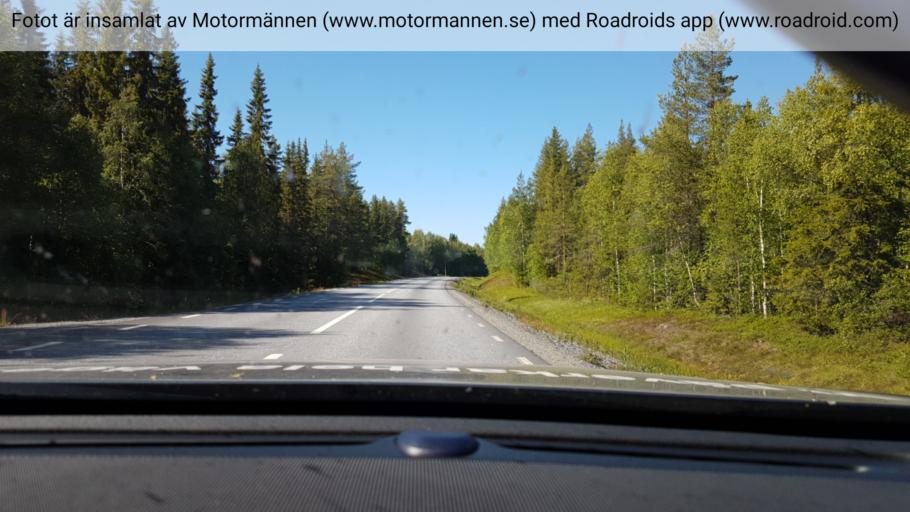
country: SE
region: Vaesterbotten
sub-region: Vilhelmina Kommun
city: Vilhelmina
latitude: 64.4658
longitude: 16.8025
